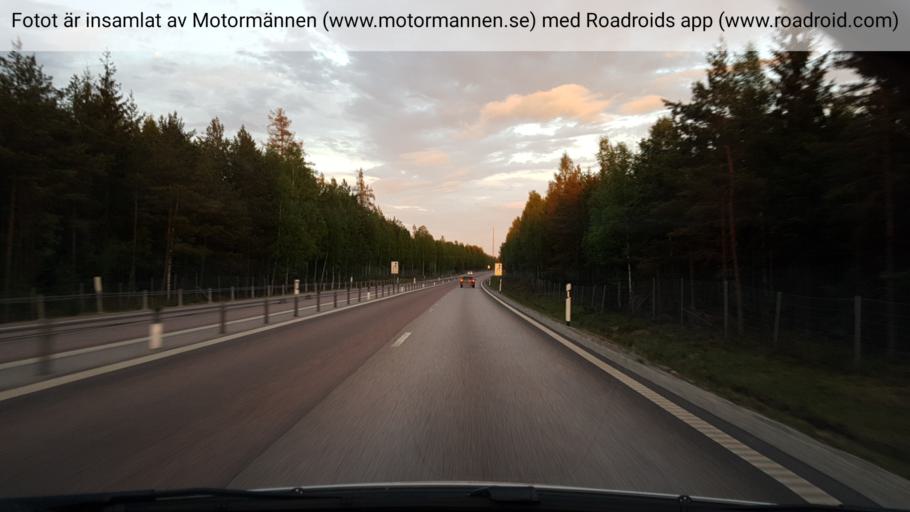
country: SE
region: Vaestmanland
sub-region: Surahammars Kommun
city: Ramnas
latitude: 59.8168
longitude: 16.1228
